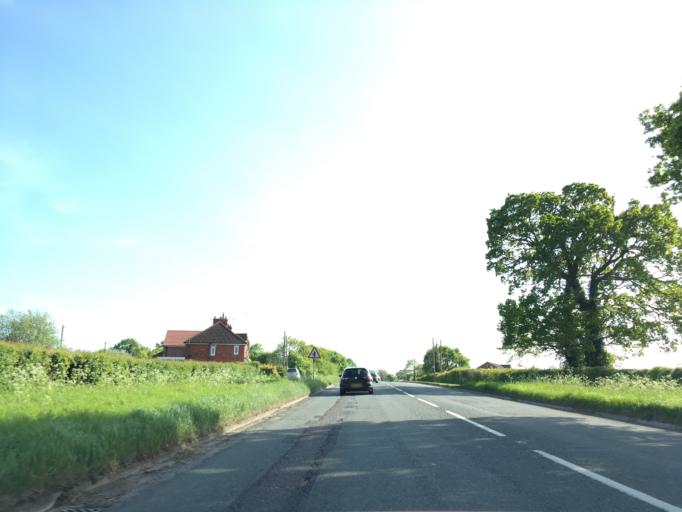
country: GB
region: England
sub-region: Gloucestershire
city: Berkeley
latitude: 51.6676
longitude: -2.4399
